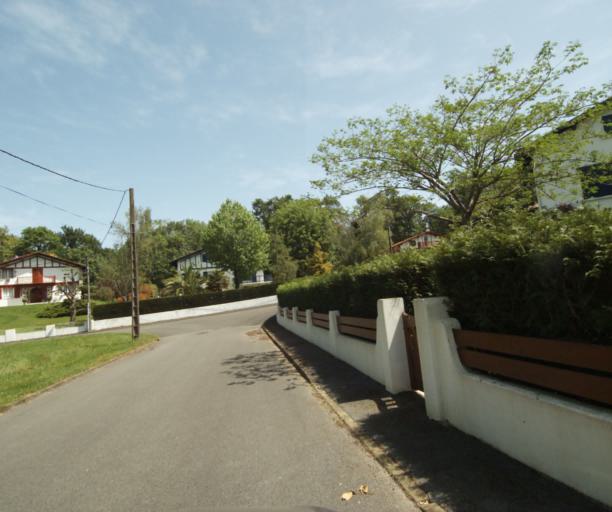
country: FR
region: Aquitaine
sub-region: Departement des Pyrenees-Atlantiques
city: Mouguerre
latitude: 43.4658
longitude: -1.4360
